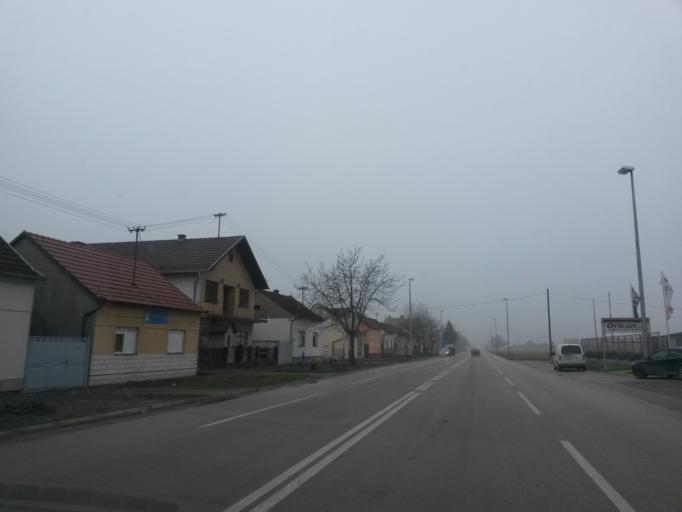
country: HR
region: Vukovarsko-Srijemska
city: Zupanja
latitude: 45.0831
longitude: 18.6959
